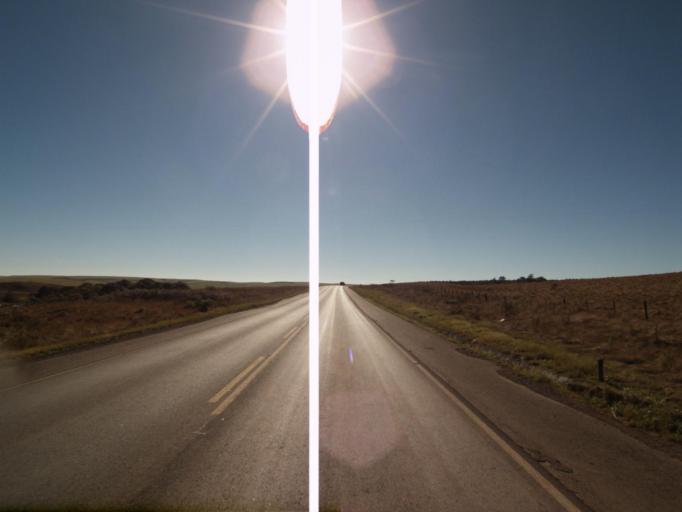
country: BR
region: Parana
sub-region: Palmas
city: Palmas
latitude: -26.7450
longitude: -51.6588
